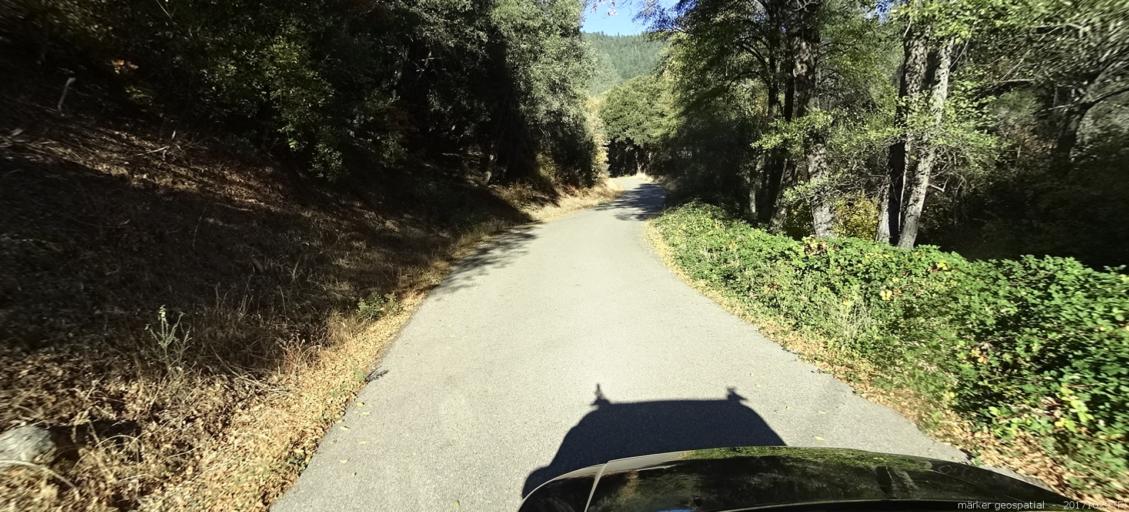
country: US
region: California
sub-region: Trinity County
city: Hayfork
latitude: 40.3844
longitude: -122.9826
